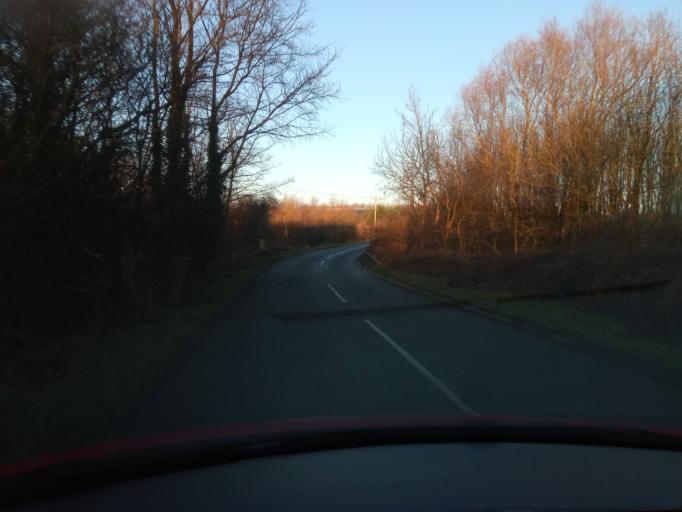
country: GB
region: England
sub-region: Leicestershire
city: Sileby
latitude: 52.7653
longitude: -1.1119
